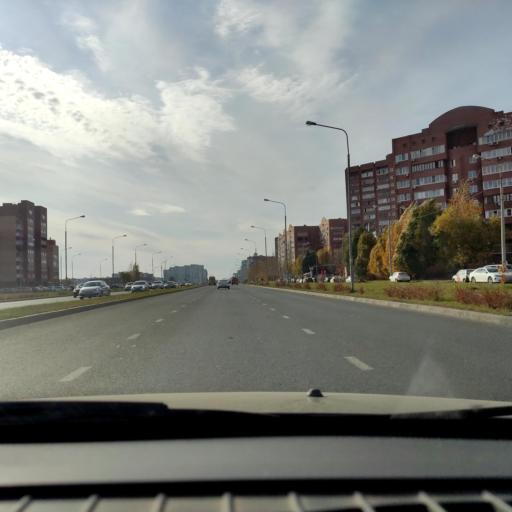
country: RU
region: Samara
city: Tol'yatti
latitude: 53.5374
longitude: 49.3551
